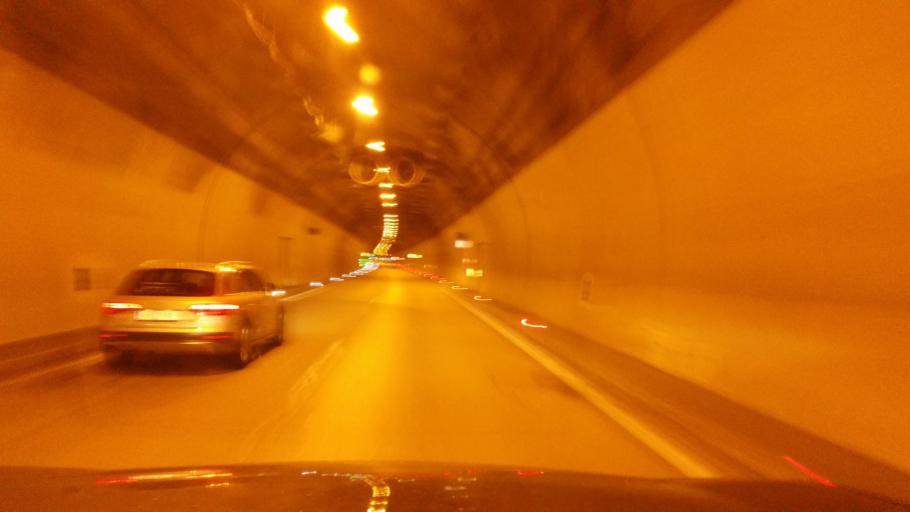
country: AT
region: Styria
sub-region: Politischer Bezirk Voitsberg
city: Modriach
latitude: 46.9653
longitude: 15.0183
